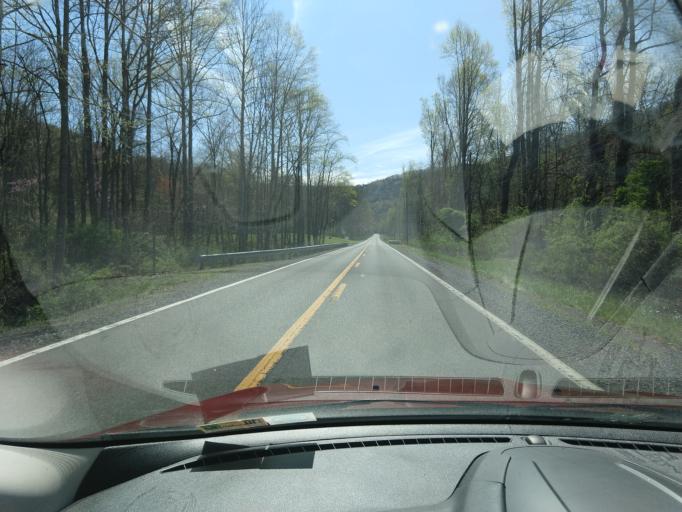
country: US
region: West Virginia
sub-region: Greenbrier County
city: Alderson
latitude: 37.7238
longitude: -80.6290
